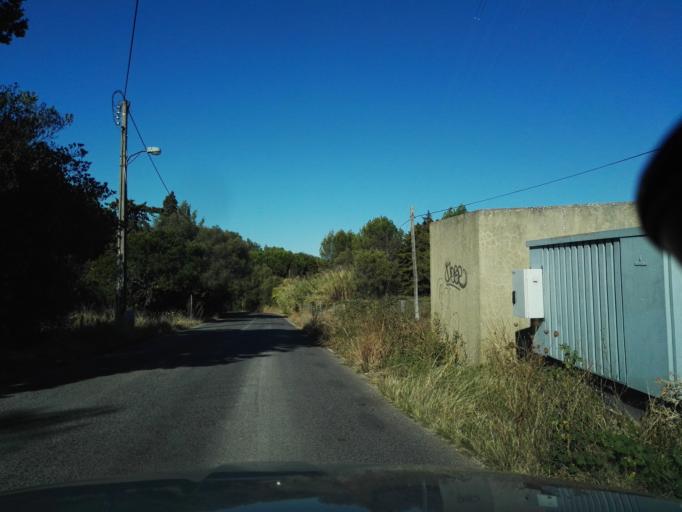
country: PT
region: Lisbon
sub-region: Odivelas
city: Pontinha
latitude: 38.7328
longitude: -9.1940
